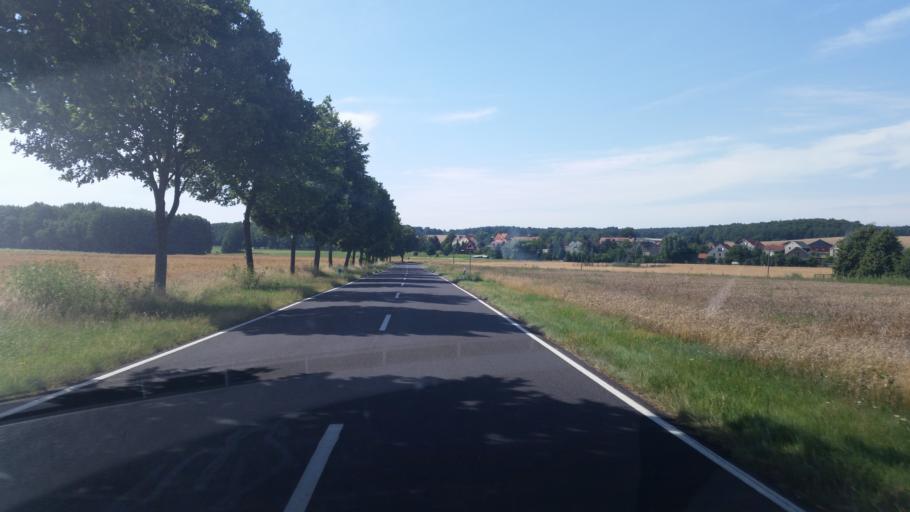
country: DE
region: Saxony
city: Kamenz
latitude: 51.2852
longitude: 14.0616
